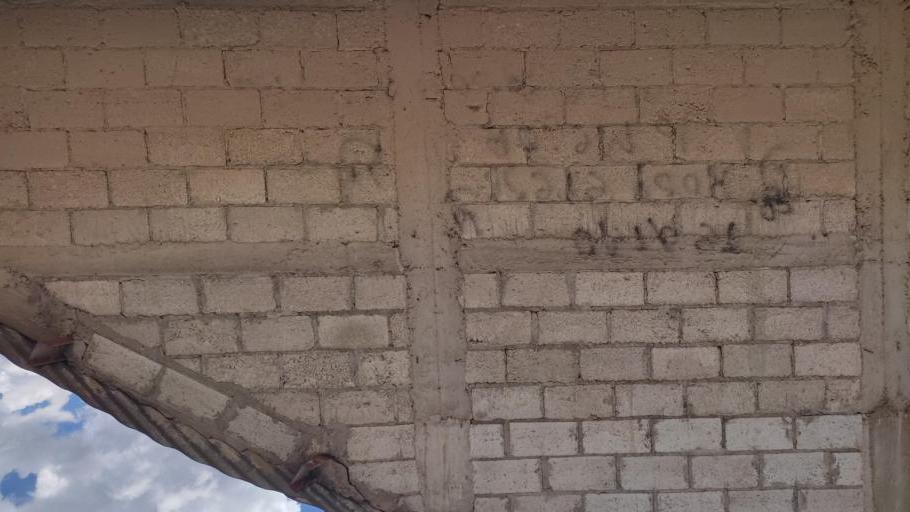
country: GT
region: Quetzaltenango
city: Quetzaltenango
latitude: 14.8573
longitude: -91.5296
